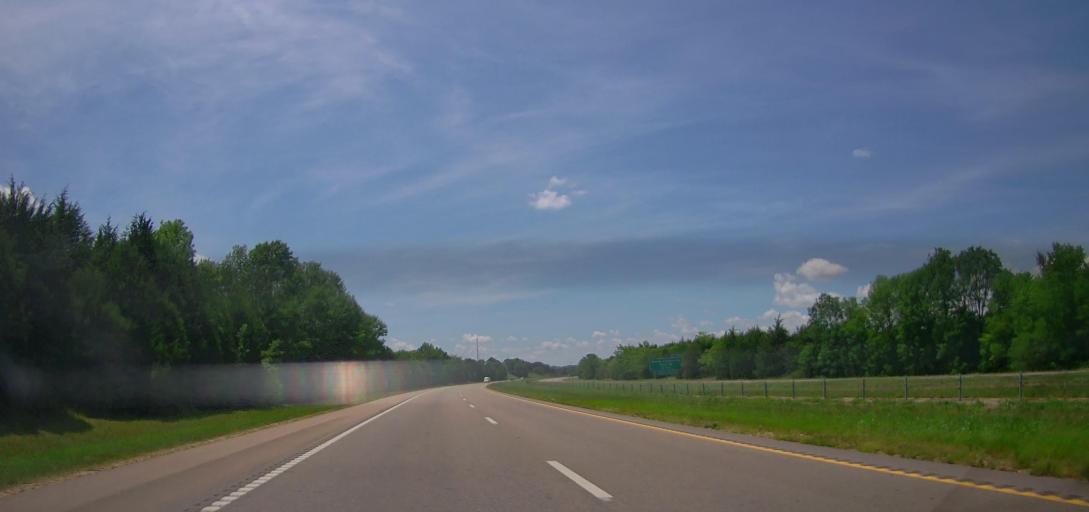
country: US
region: Mississippi
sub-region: Lee County
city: Tupelo
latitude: 34.3008
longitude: -88.7510
